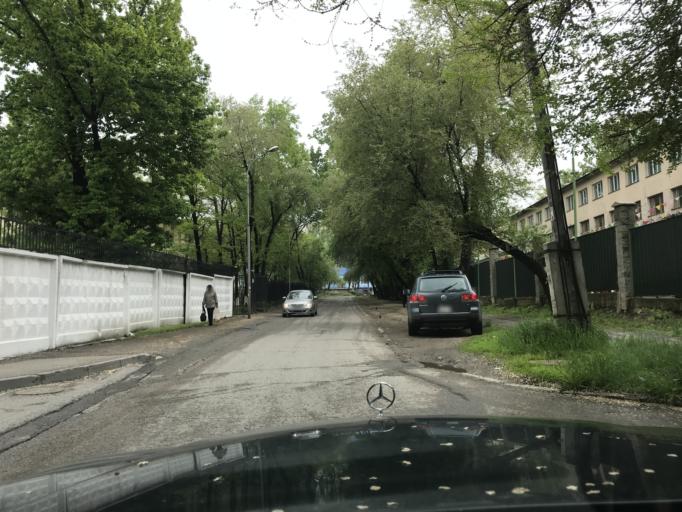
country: KZ
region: Almaty Qalasy
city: Almaty
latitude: 43.2071
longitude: 76.8703
